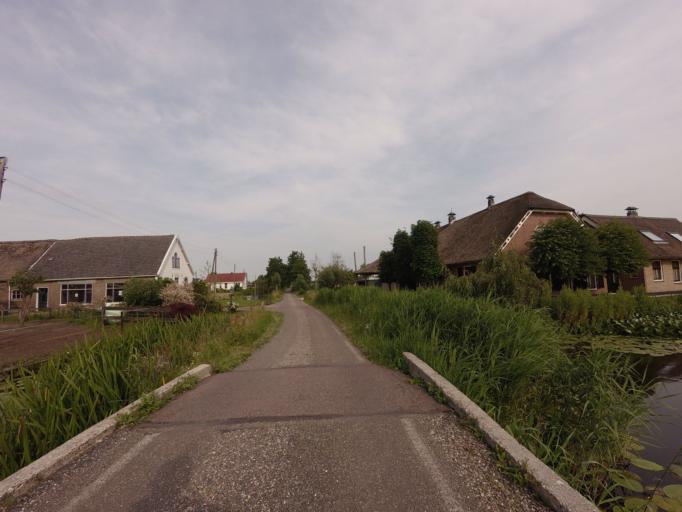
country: NL
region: South Holland
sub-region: Bodegraven-Reeuwijk
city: Bodegraven
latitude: 52.0499
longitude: 4.7715
